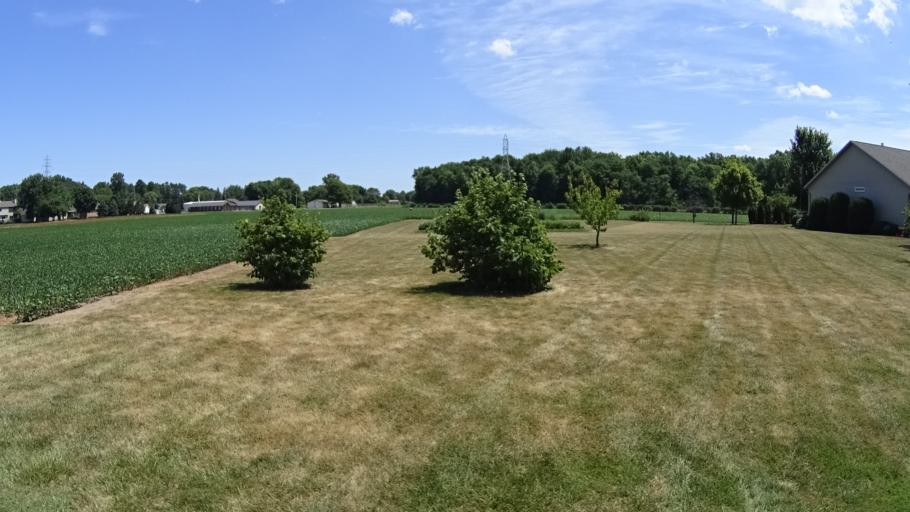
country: US
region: Ohio
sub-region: Erie County
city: Sandusky
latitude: 41.3944
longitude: -82.6960
